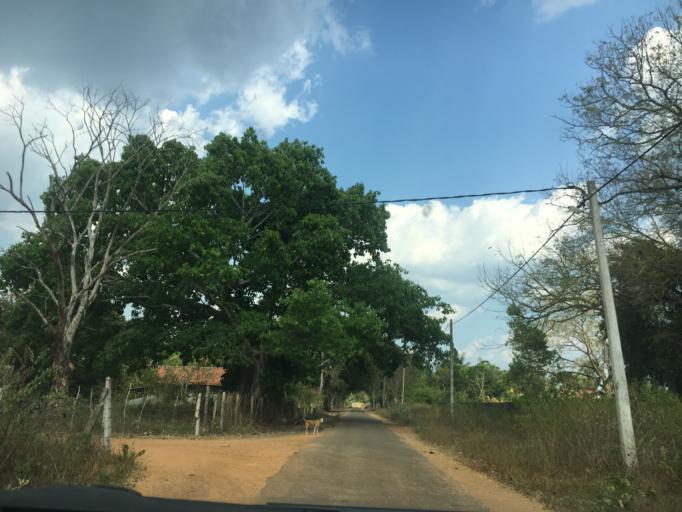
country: LK
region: Northern Province
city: Kilinochchi
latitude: 9.1407
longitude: 80.4433
